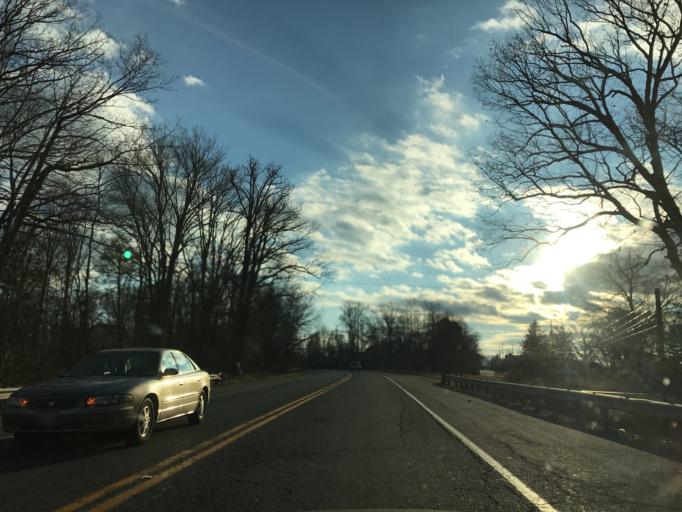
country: US
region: Maryland
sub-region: Cecil County
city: North East
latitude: 39.6483
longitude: -75.9567
